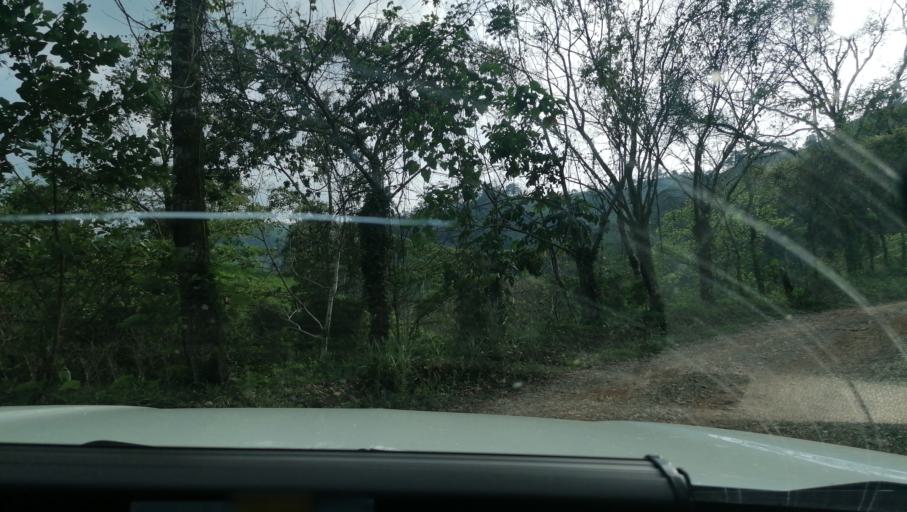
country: MX
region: Chiapas
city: Ixtacomitan
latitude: 17.3322
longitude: -93.1040
